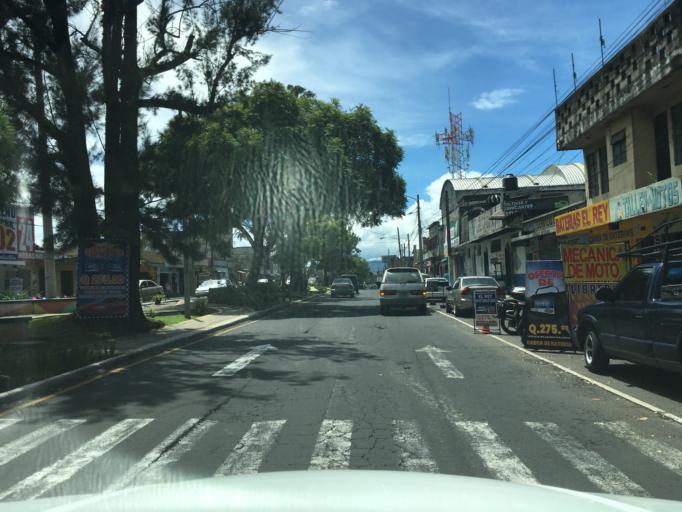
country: GT
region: Guatemala
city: Guatemala City
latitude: 14.6284
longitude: -90.5449
